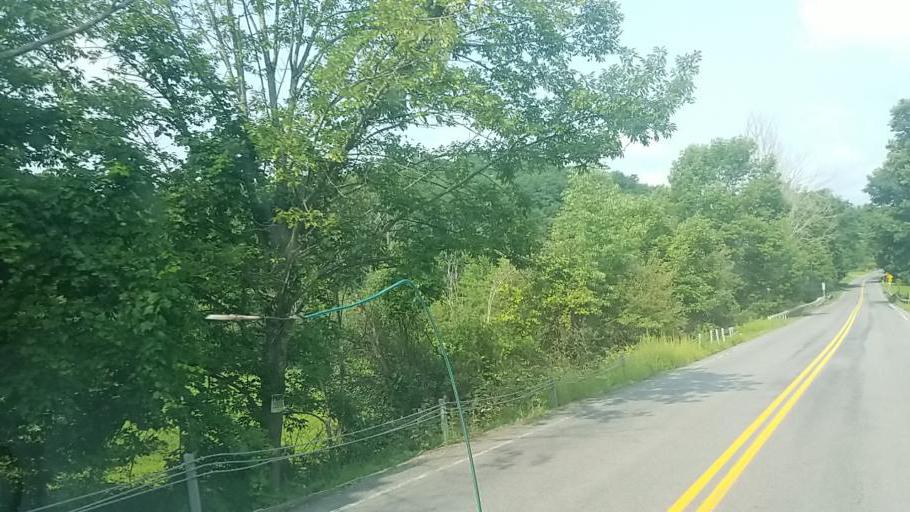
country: US
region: New York
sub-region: Montgomery County
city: Fonda
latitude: 42.9902
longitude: -74.4397
